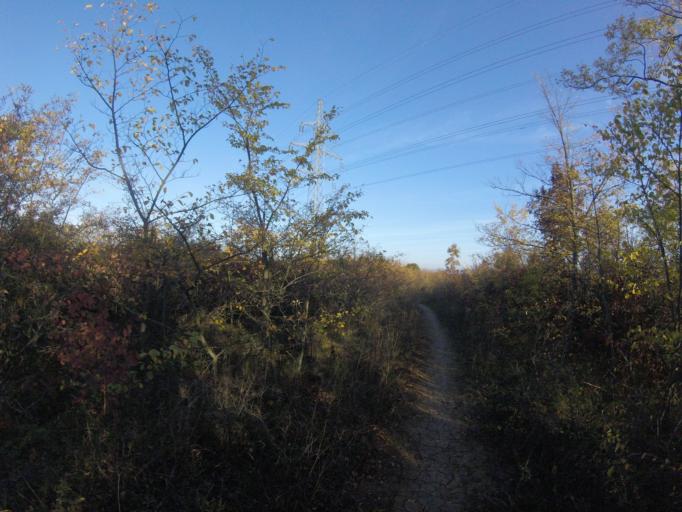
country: HU
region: Pest
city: Urom
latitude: 47.5981
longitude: 19.0312
